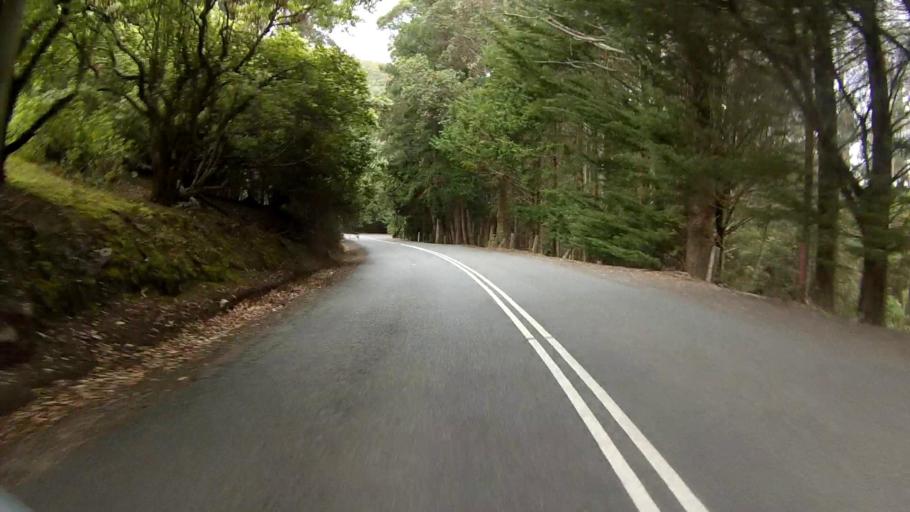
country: AU
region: Tasmania
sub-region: Hobart
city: Dynnyrne
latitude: -42.9295
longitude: 147.2480
